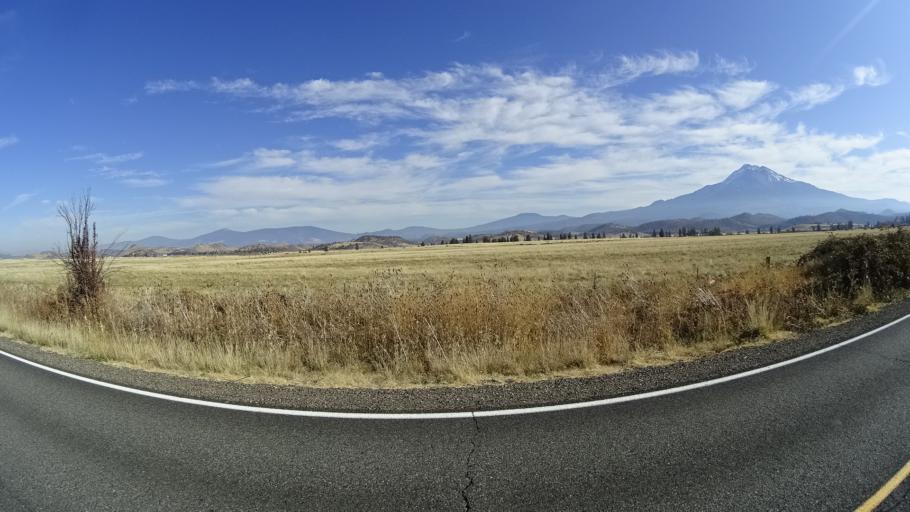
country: US
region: California
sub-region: Siskiyou County
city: Weed
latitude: 41.4613
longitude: -122.4634
